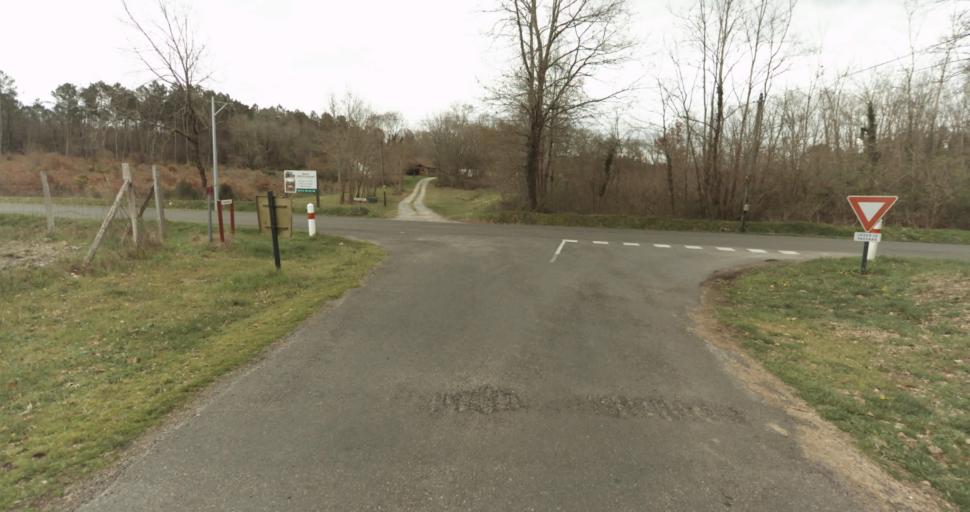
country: FR
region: Aquitaine
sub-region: Departement des Landes
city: Roquefort
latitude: 44.0426
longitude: -0.3078
